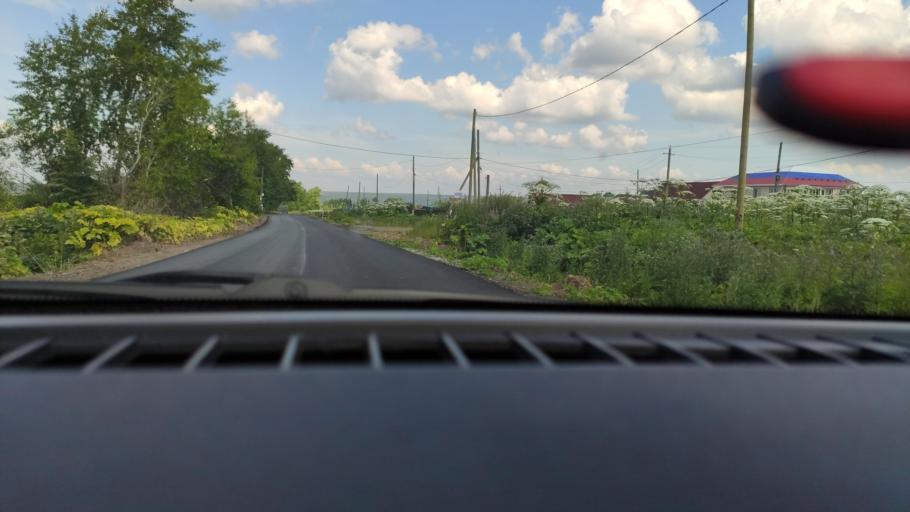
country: RU
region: Perm
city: Sylva
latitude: 58.0384
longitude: 56.7247
